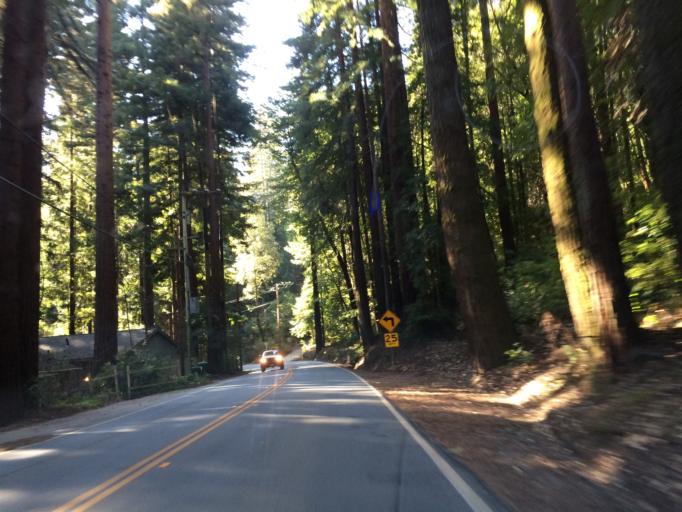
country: US
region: California
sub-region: Santa Cruz County
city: Boulder Creek
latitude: 37.1411
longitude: -122.1527
